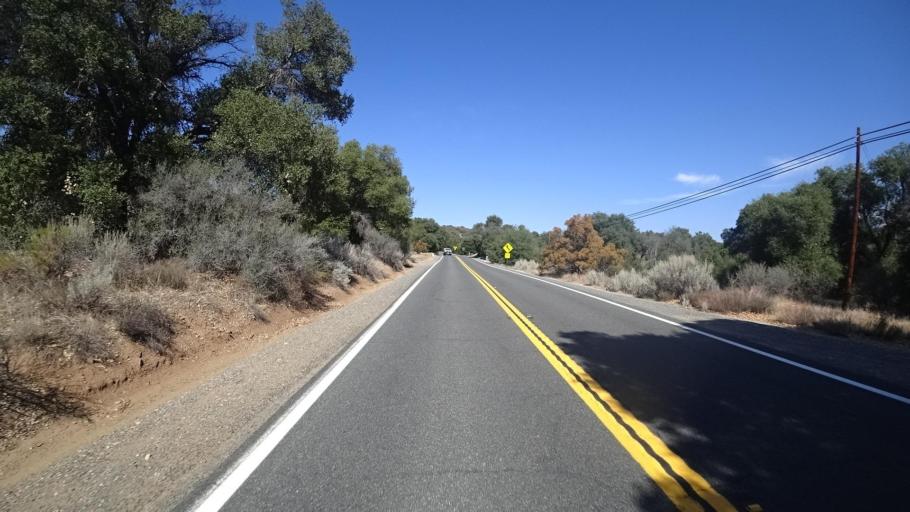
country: US
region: California
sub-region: Riverside County
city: Aguanga
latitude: 33.3178
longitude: -116.6955
